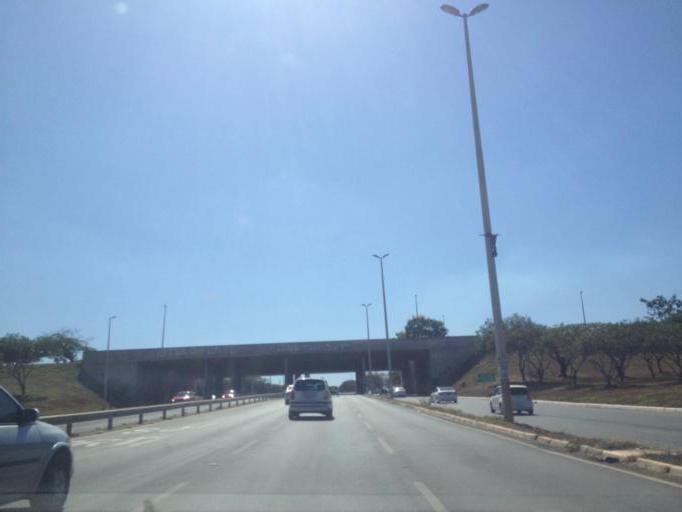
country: BR
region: Federal District
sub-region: Brasilia
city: Brasilia
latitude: -15.8465
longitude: -47.9314
